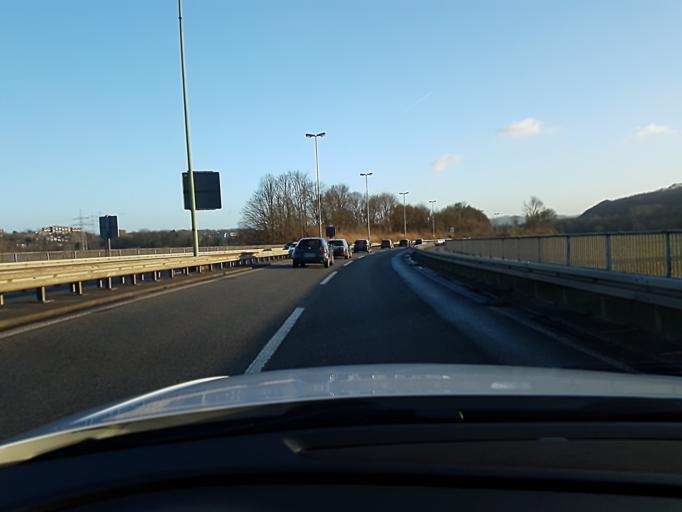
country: DE
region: North Rhine-Westphalia
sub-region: Regierungsbezirk Dusseldorf
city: Essen
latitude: 51.4278
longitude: 7.0583
